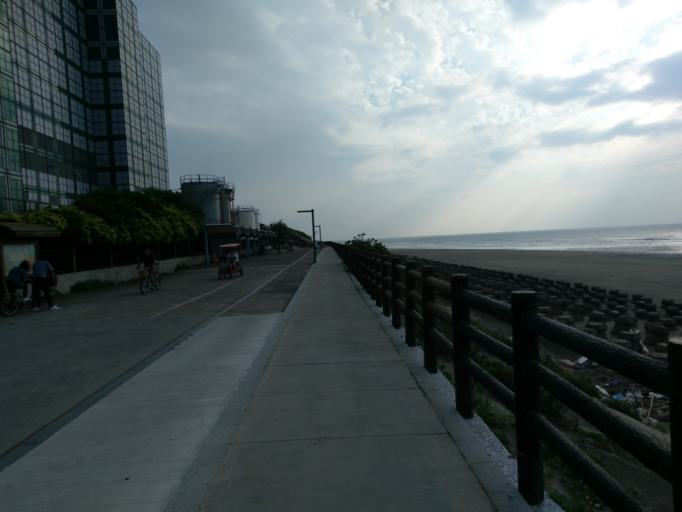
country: TW
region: Taiwan
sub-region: Hsinchu
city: Hsinchu
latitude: 24.8353
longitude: 120.9165
